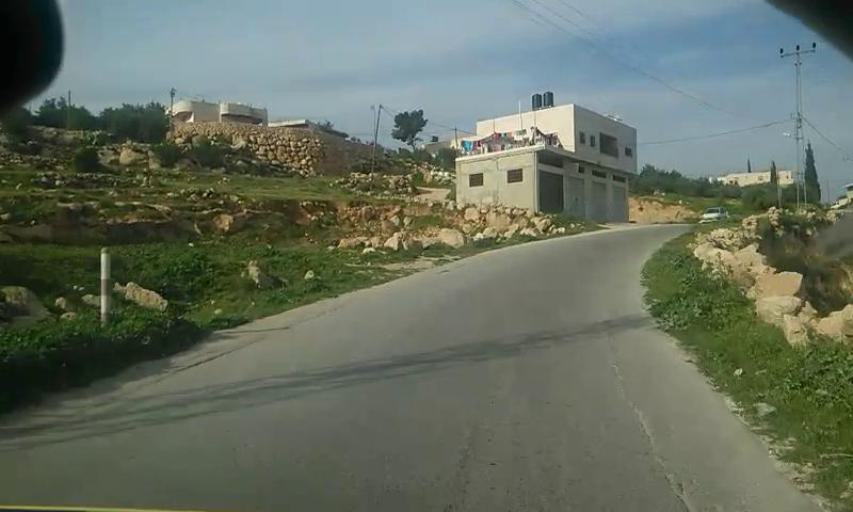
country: PS
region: West Bank
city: Bayt Ula
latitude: 31.5862
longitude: 35.0235
